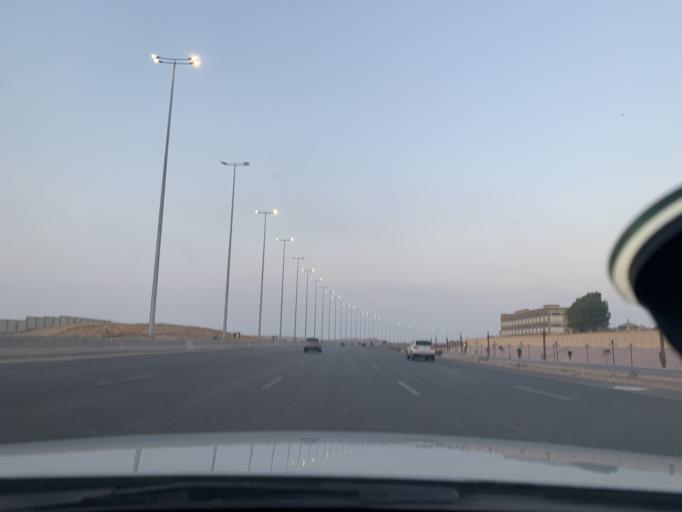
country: EG
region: Muhafazat al Qalyubiyah
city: Al Khankah
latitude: 30.0933
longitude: 31.4760
